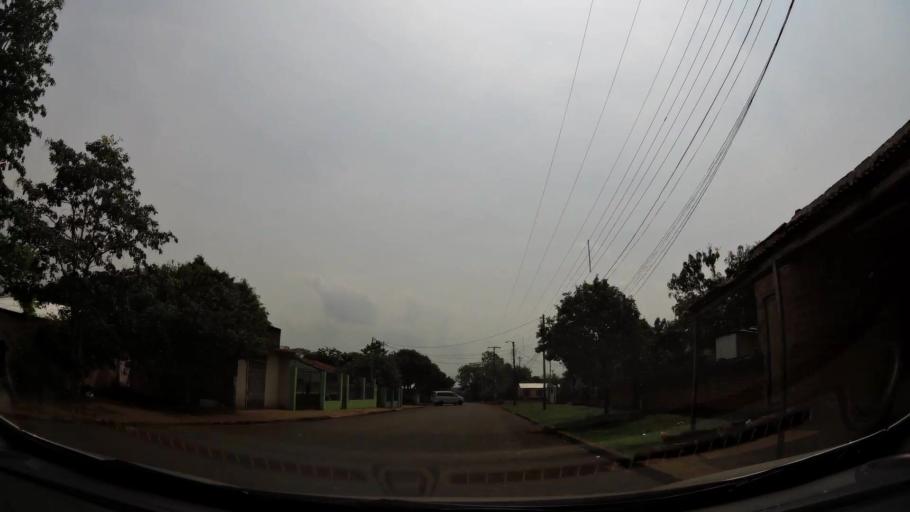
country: BR
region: Parana
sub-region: Foz Do Iguacu
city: Foz do Iguacu
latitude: -25.5715
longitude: -54.6124
